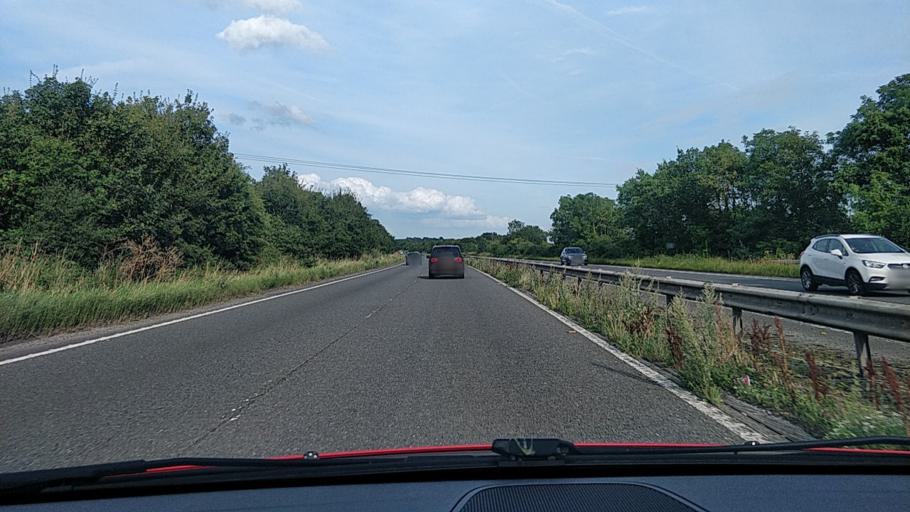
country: GB
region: England
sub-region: Cheshire West and Chester
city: Eccleston
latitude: 53.1564
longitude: -2.9260
